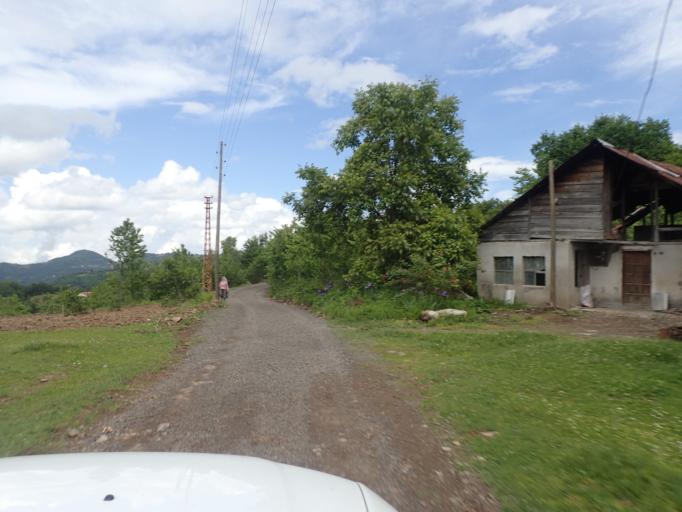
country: TR
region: Ordu
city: Akkus
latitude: 40.9157
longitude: 36.8925
